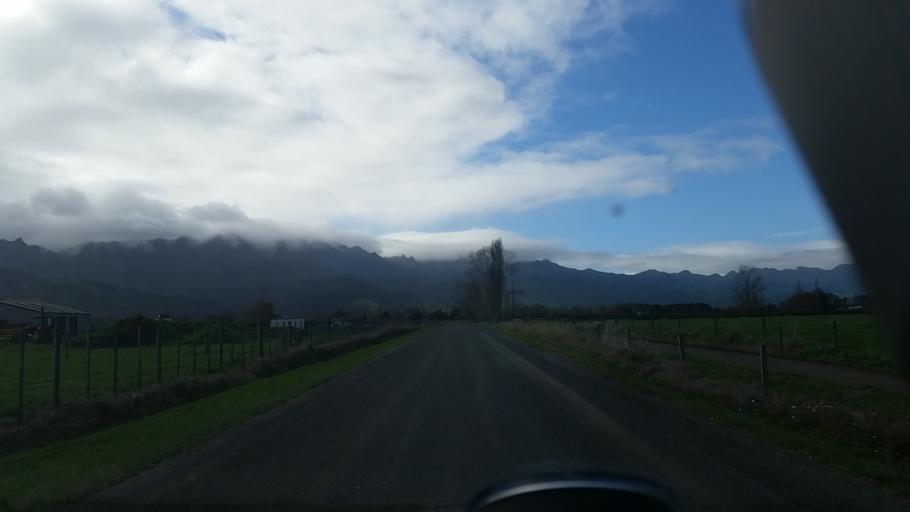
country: NZ
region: Bay of Plenty
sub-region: Western Bay of Plenty District
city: Katikati
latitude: -37.5775
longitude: 175.7235
